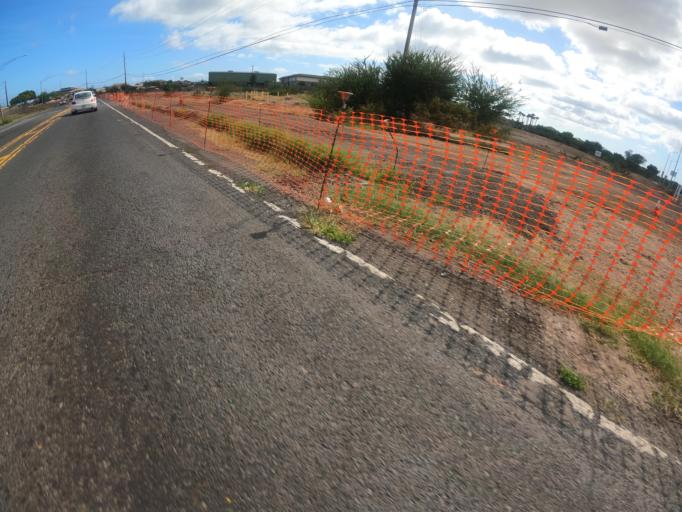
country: US
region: Hawaii
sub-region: Honolulu County
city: Makakilo City
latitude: 21.3292
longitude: -158.0716
